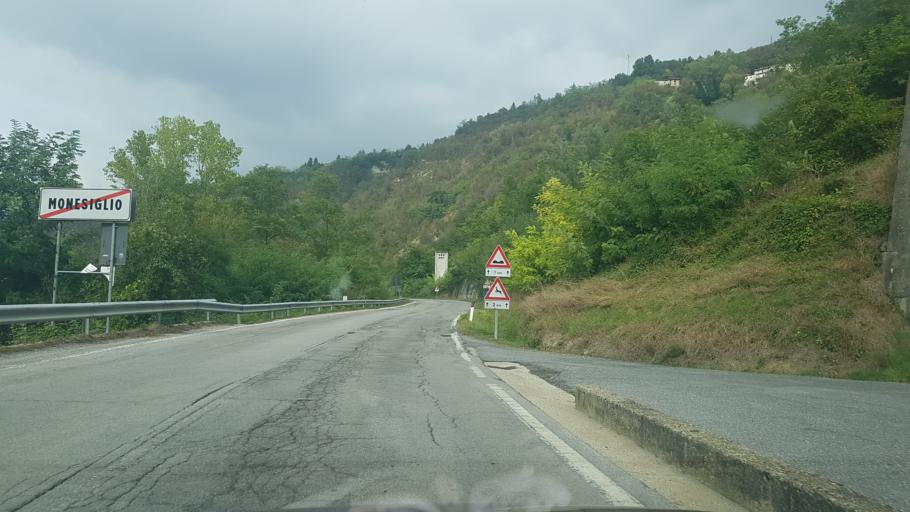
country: IT
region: Piedmont
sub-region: Provincia di Cuneo
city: Monesiglio
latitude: 44.4689
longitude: 8.1170
